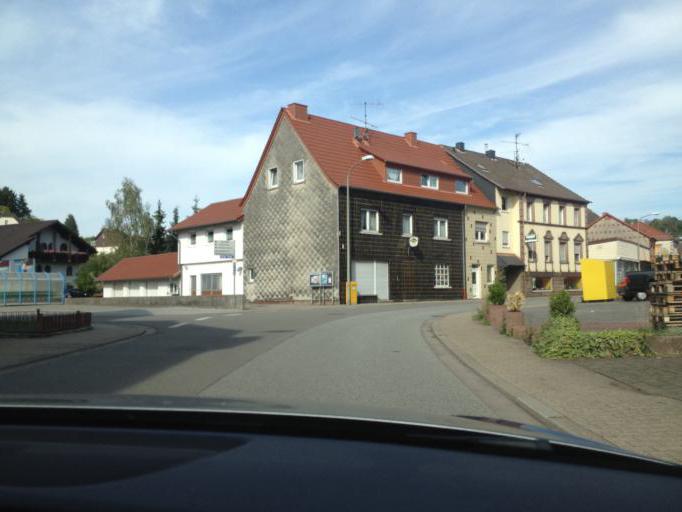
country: DE
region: Rheinland-Pfalz
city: Breitenbach
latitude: 49.4336
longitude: 7.2696
